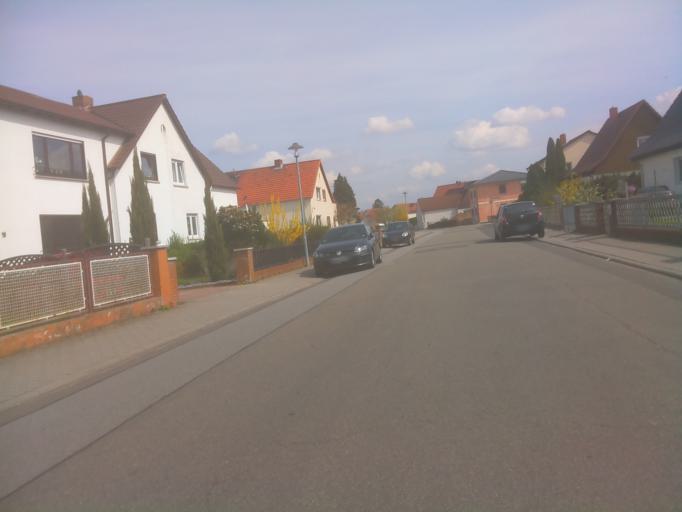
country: DE
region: Hesse
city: Lampertheim
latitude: 49.6047
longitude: 8.4590
